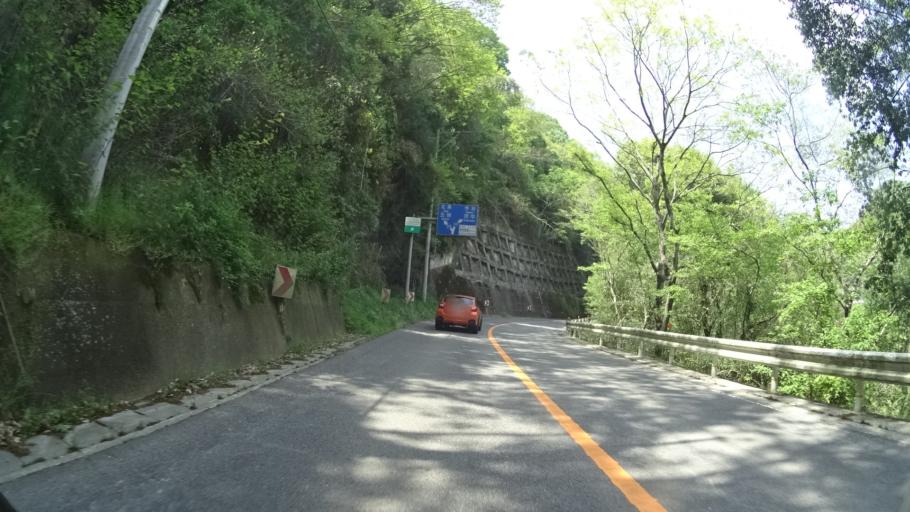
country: JP
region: Ehime
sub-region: Shikoku-chuo Shi
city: Matsuyama
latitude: 33.8880
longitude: 132.8362
